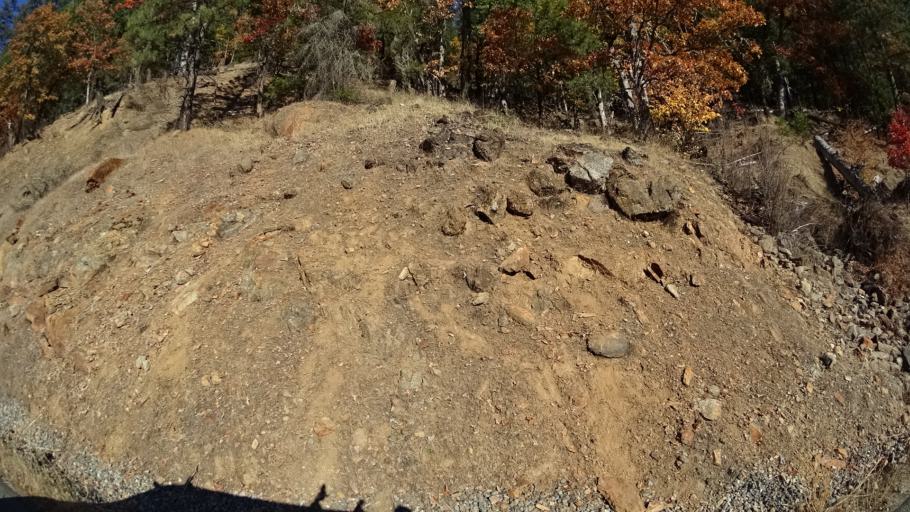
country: US
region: California
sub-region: Siskiyou County
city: Happy Camp
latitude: 41.6342
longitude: -123.0911
